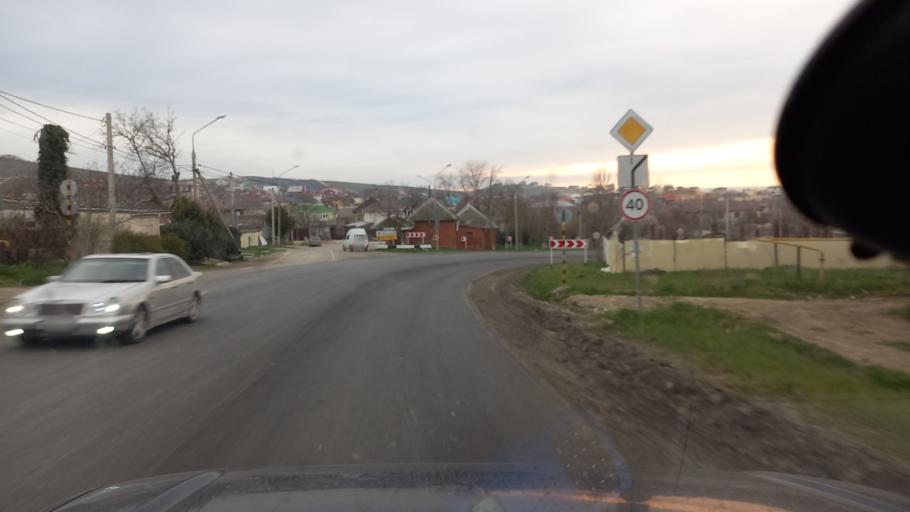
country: RU
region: Krasnodarskiy
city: Anapskaya
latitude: 44.8516
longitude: 37.3646
